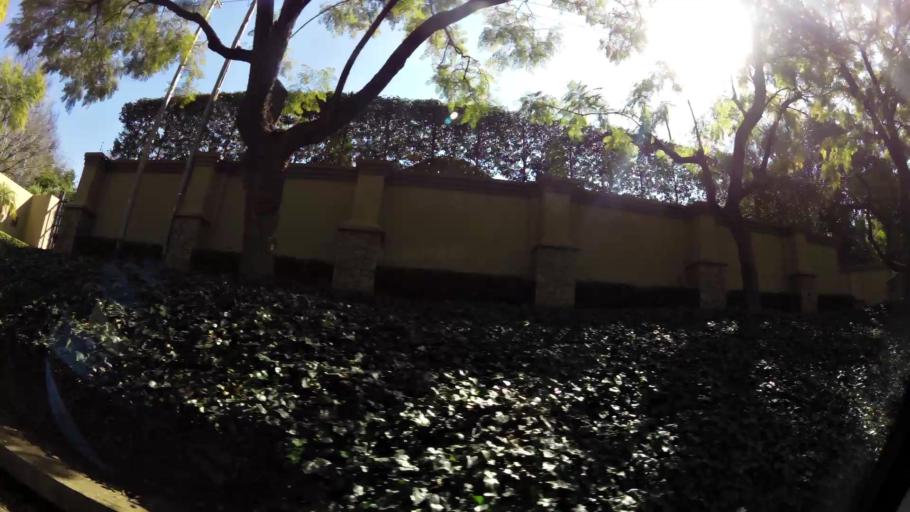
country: ZA
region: Gauteng
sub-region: City of Tshwane Metropolitan Municipality
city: Pretoria
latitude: -25.7862
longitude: 28.2469
